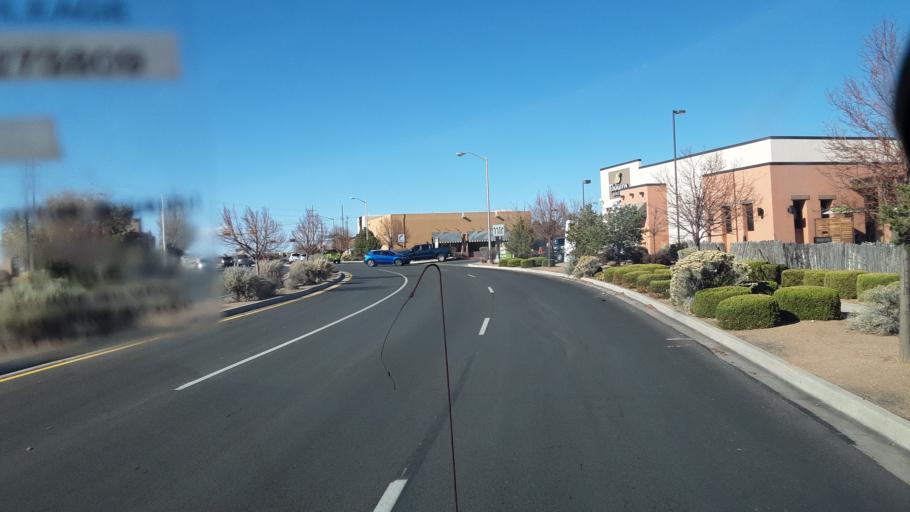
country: US
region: New Mexico
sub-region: Santa Fe County
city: Agua Fria
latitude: 35.6410
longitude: -106.0117
